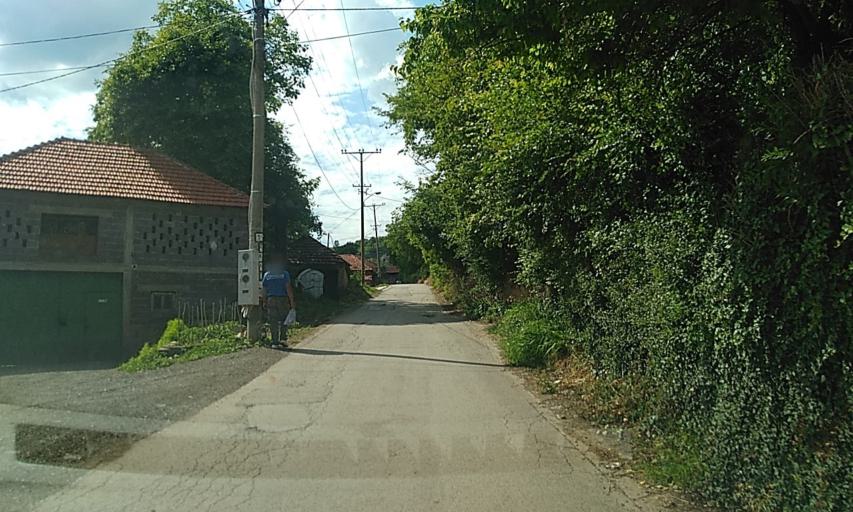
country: RS
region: Central Serbia
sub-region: Nisavski Okrug
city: Niska Banja
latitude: 43.3618
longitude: 22.0349
